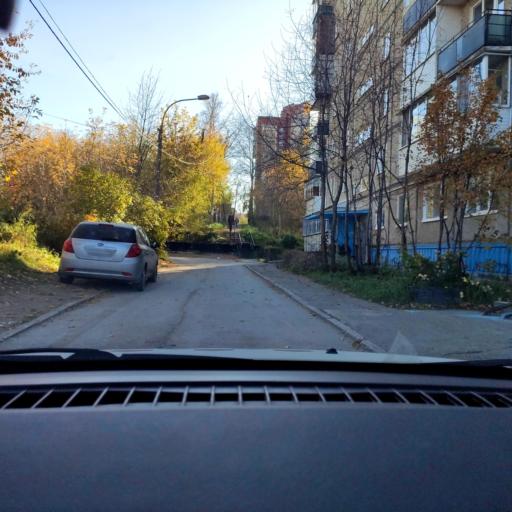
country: RU
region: Perm
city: Perm
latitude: 58.1135
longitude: 56.3769
